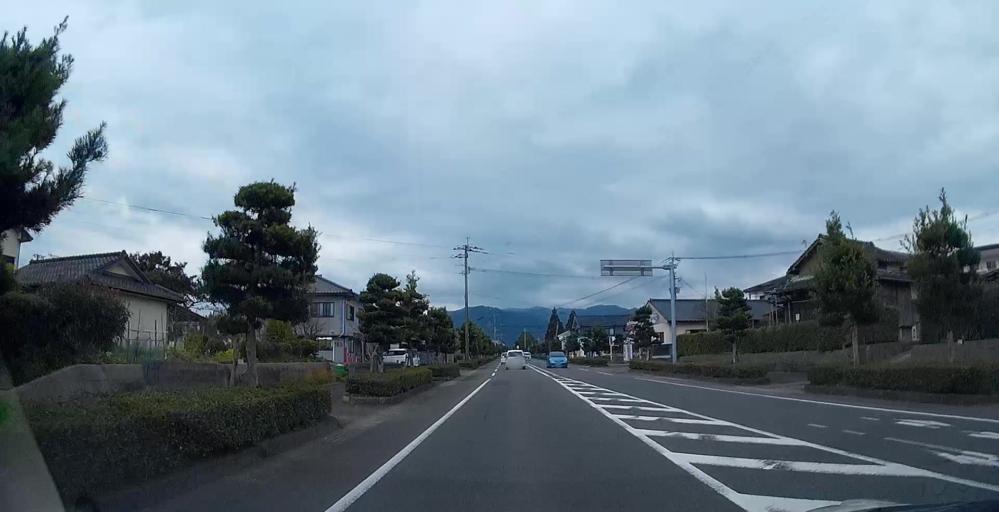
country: JP
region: Kagoshima
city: Izumi
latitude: 32.0865
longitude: 130.3434
